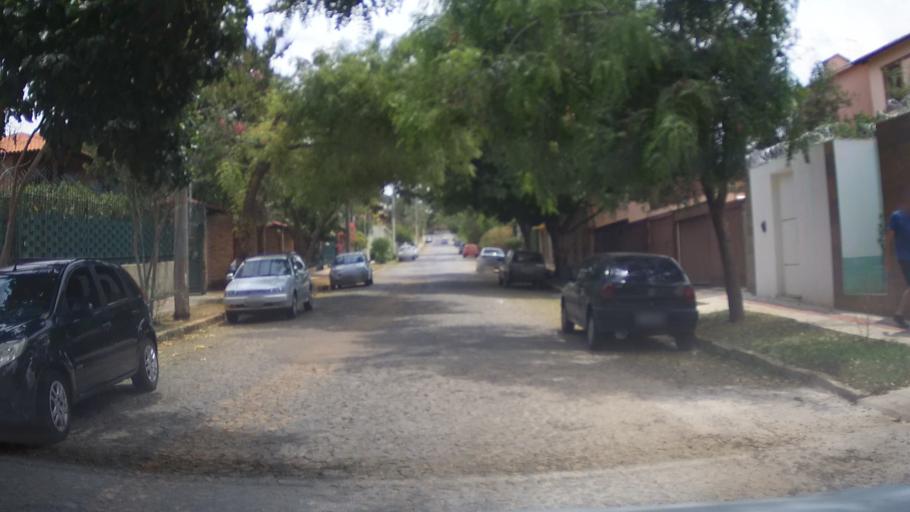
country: BR
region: Minas Gerais
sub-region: Belo Horizonte
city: Belo Horizonte
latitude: -19.8586
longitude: -43.9676
